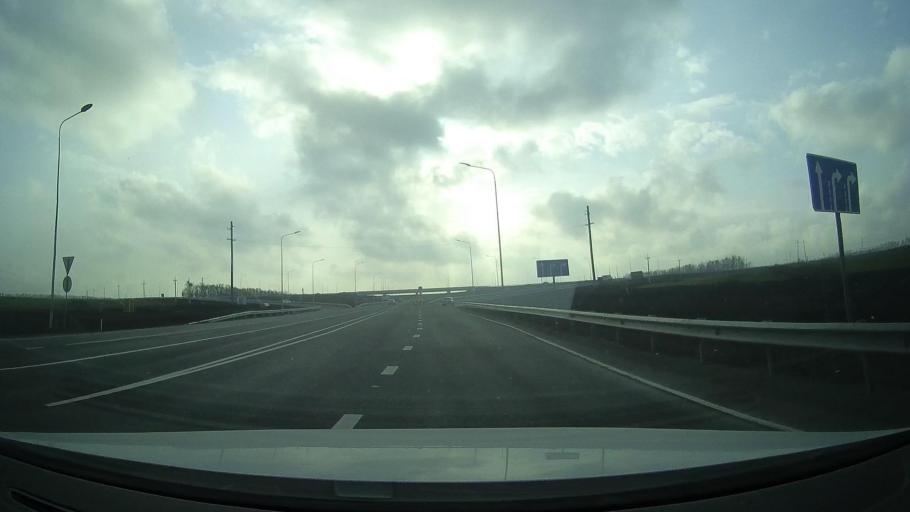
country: RU
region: Rostov
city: Grushevskaya
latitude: 47.3818
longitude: 39.8453
